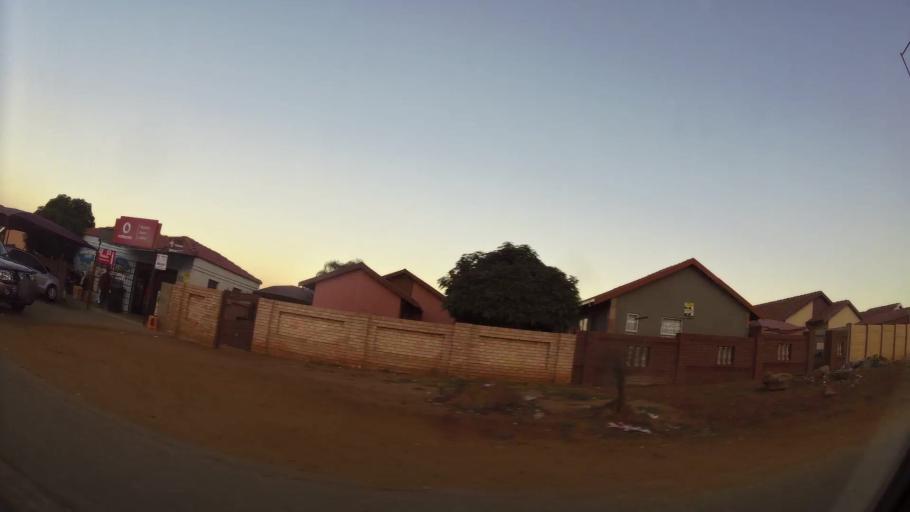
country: ZA
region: North-West
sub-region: Bojanala Platinum District Municipality
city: Rustenburg
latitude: -25.6499
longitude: 27.2057
